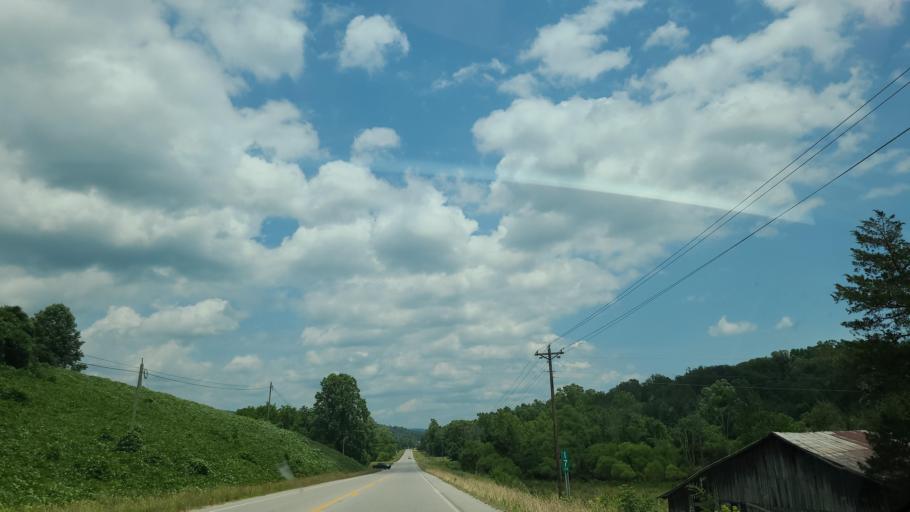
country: US
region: Tennessee
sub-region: Bledsoe County
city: Pikeville
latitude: 35.6370
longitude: -85.1719
